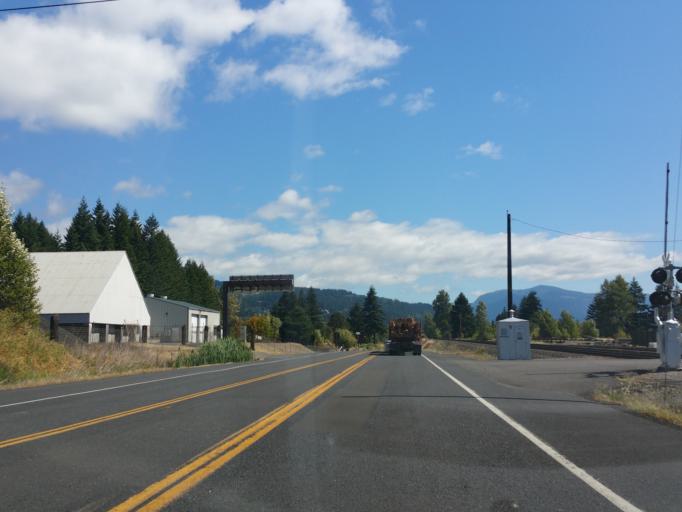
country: US
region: Oregon
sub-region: Hood River County
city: Cascade Locks
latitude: 45.6824
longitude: -121.9014
